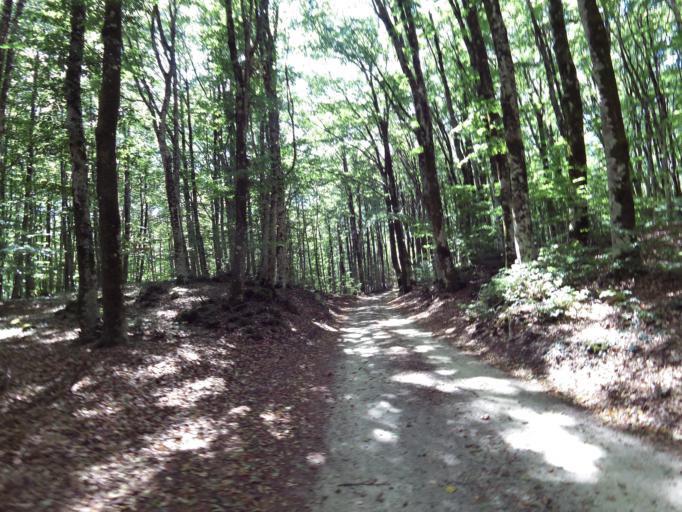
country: IT
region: Calabria
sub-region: Provincia di Vibo-Valentia
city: Mongiana
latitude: 38.5161
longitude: 16.3461
